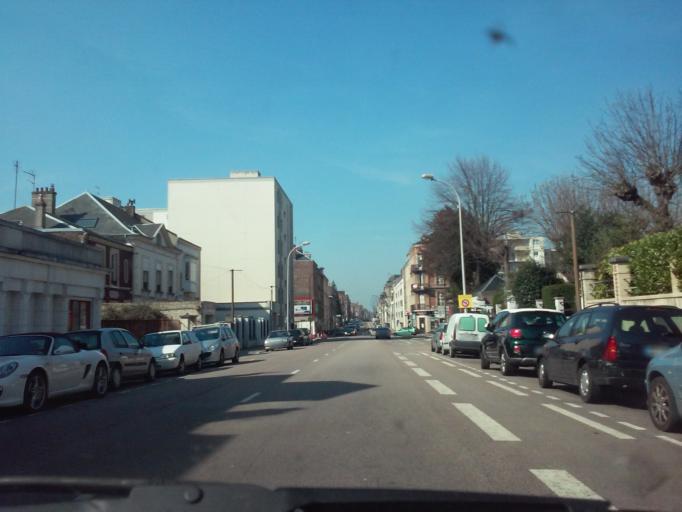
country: FR
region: Haute-Normandie
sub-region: Departement de la Seine-Maritime
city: Fontaine-la-Mallet
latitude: 49.5016
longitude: 0.1515
